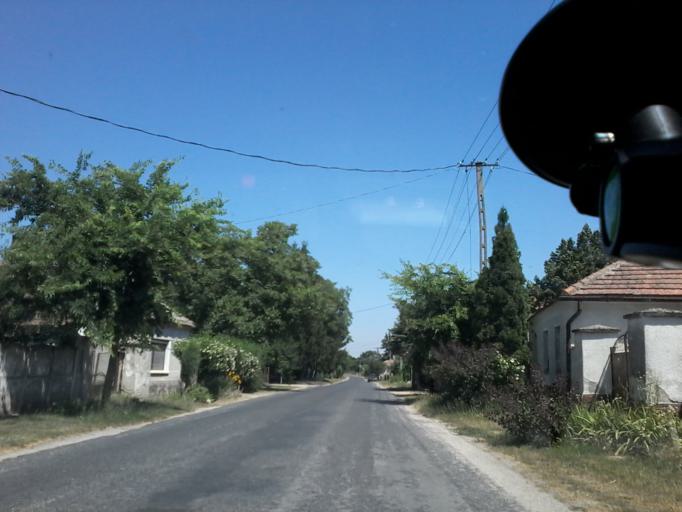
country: HU
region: Vas
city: Janoshaza
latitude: 47.1673
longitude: 17.1172
